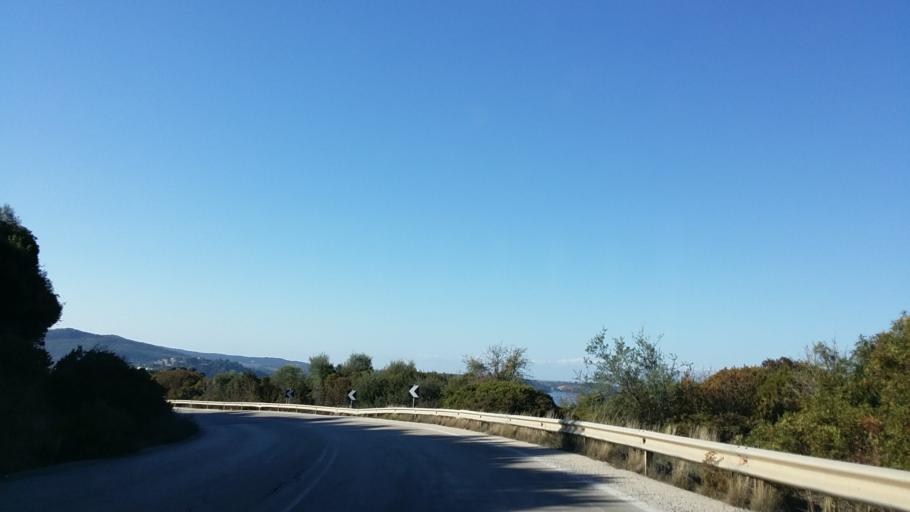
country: GR
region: West Greece
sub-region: Nomos Aitolias kai Akarnanias
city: Vonitsa
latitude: 38.9289
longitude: 20.9169
